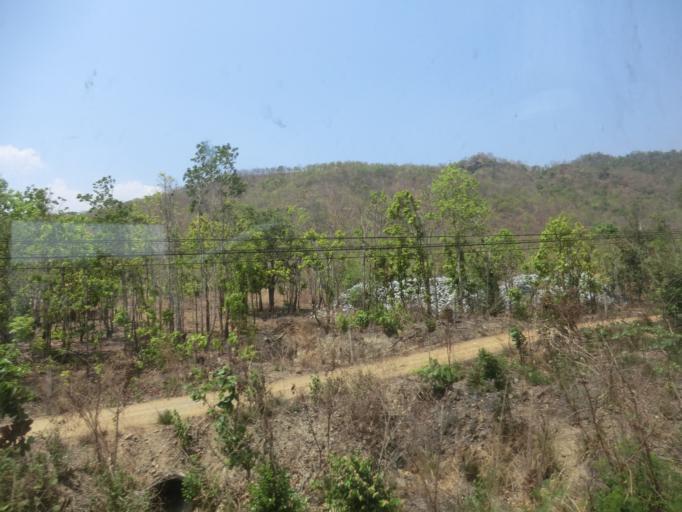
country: VN
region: Binh Thuan
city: Thuan Nam
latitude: 10.9171
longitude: 107.8550
